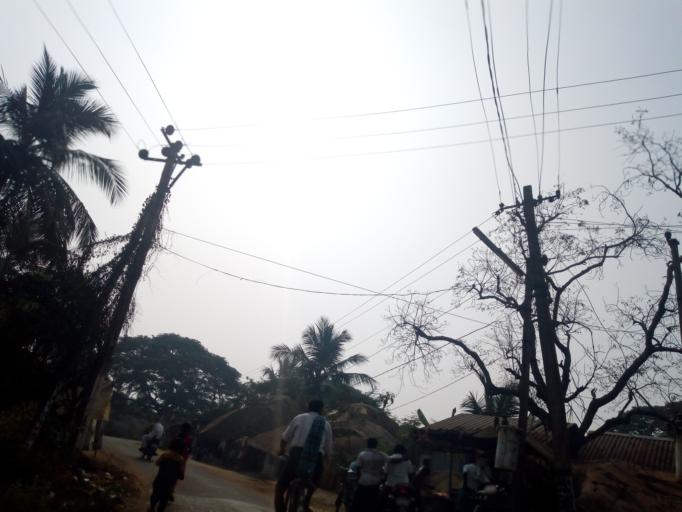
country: IN
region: Andhra Pradesh
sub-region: West Godavari
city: Tadepallegudem
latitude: 16.8122
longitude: 81.3639
